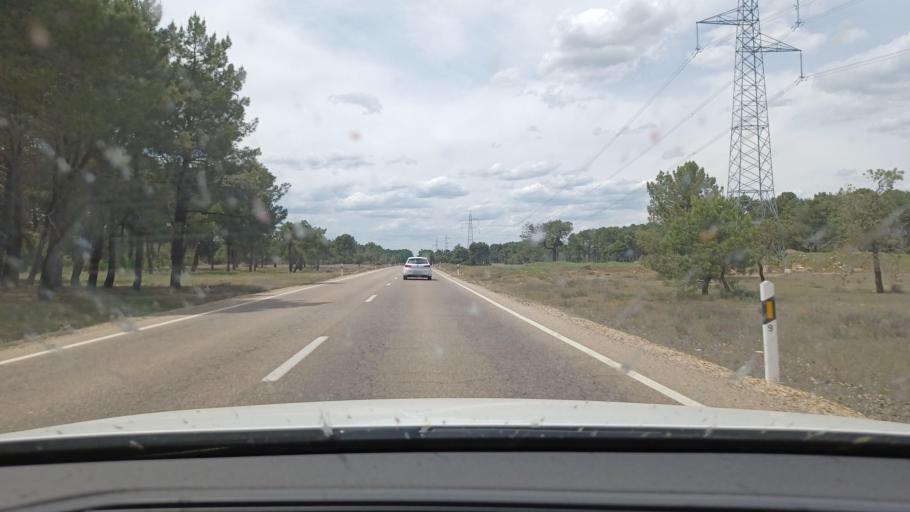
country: ES
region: Castille and Leon
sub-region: Provincia de Segovia
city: Cantalejo
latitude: 41.2914
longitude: -4.0039
